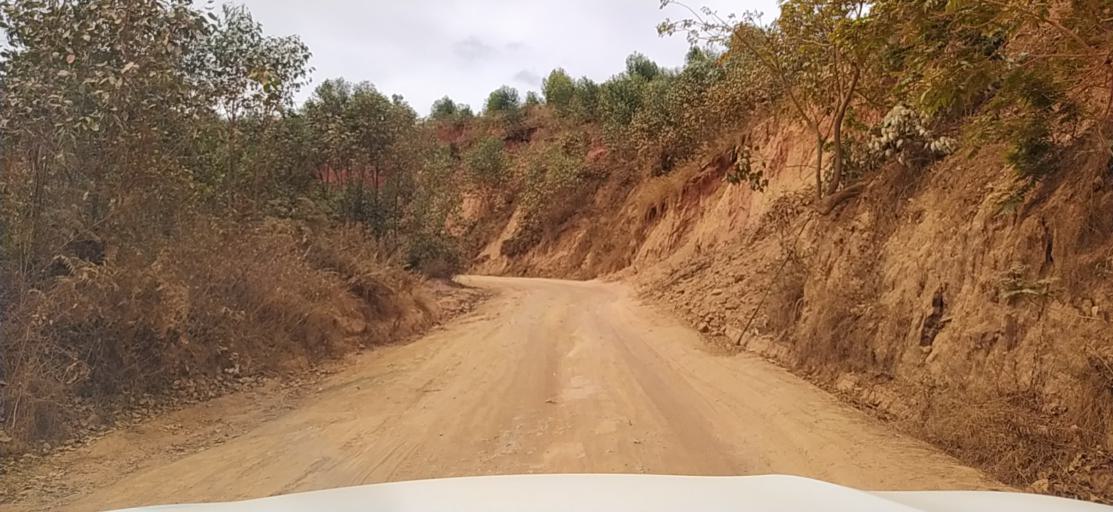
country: MG
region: Alaotra Mangoro
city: Ambatondrazaka
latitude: -17.9989
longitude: 48.2634
